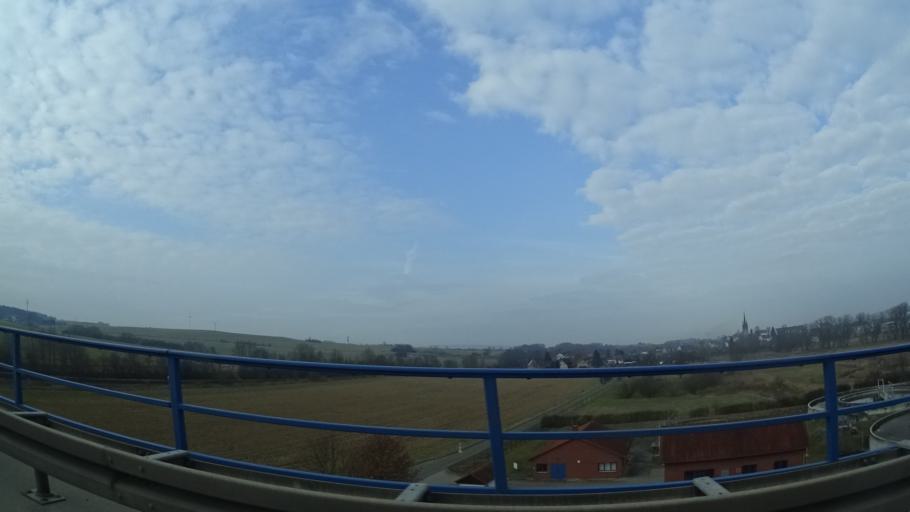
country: DE
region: Thuringia
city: Neustadt (Orla)
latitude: 50.7290
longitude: 11.7287
